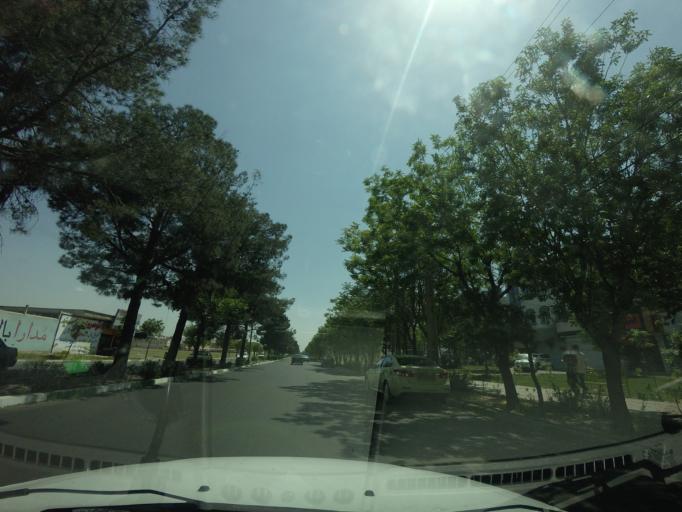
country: IR
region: Tehran
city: Eslamshahr
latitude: 35.5384
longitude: 51.2100
